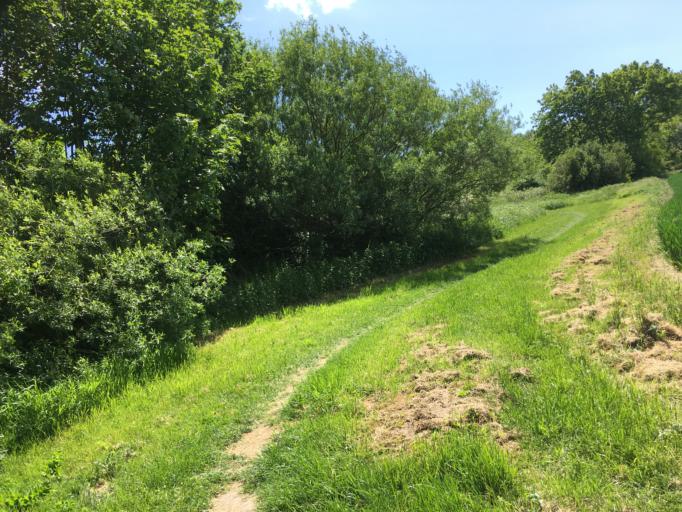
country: SE
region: Skane
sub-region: Lunds Kommun
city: Lund
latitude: 55.6856
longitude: 13.1726
